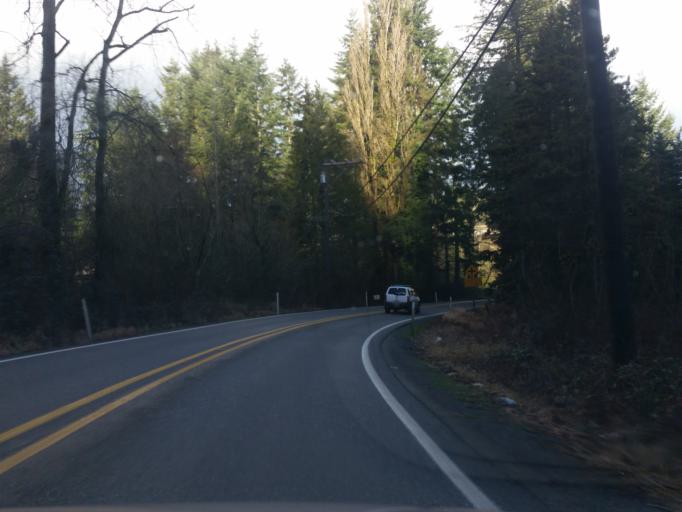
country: US
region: Washington
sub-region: Snohomish County
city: Alderwood Manor
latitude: 47.8244
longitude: -122.2571
